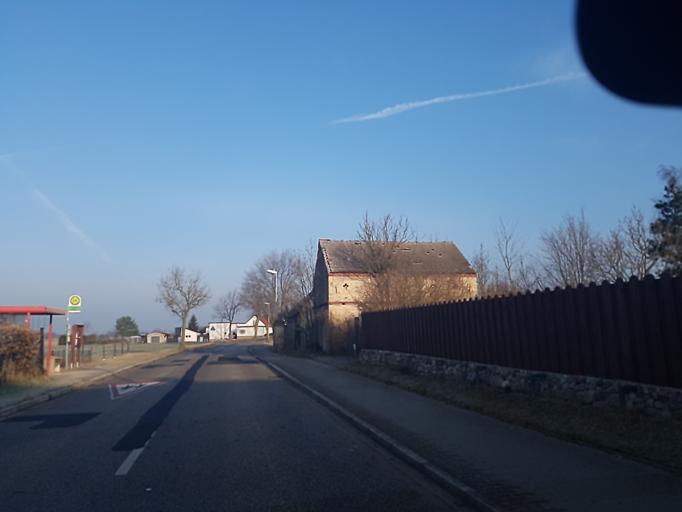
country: DE
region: Brandenburg
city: Bruck
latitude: 52.2295
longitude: 12.7142
